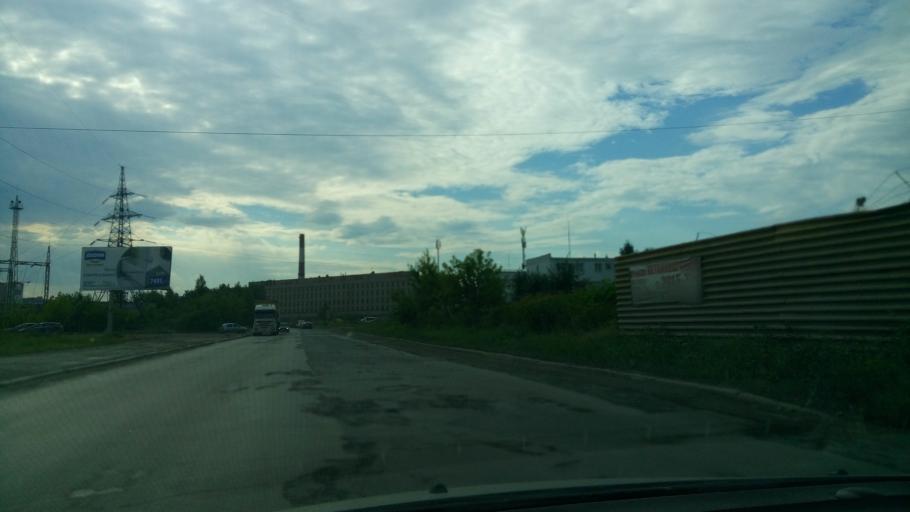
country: RU
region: Sverdlovsk
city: Yekaterinburg
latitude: 56.8873
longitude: 60.6565
